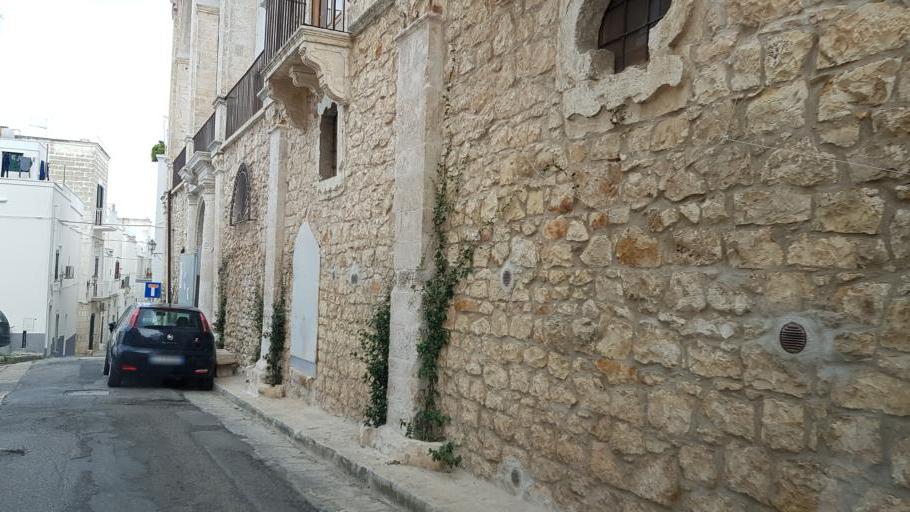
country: IT
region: Apulia
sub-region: Provincia di Brindisi
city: Ostuni
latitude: 40.7307
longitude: 17.5773
